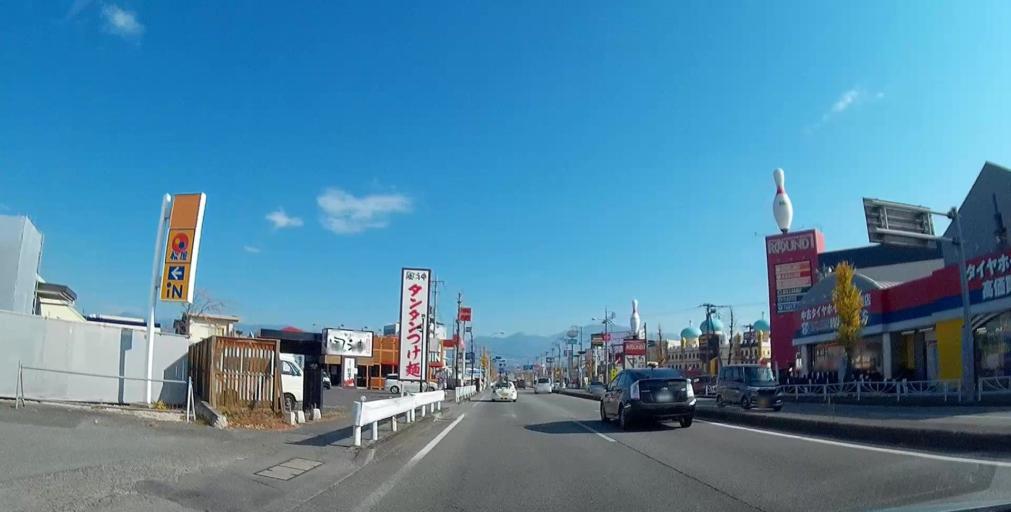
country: JP
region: Yamanashi
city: Isawa
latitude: 35.6443
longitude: 138.6222
